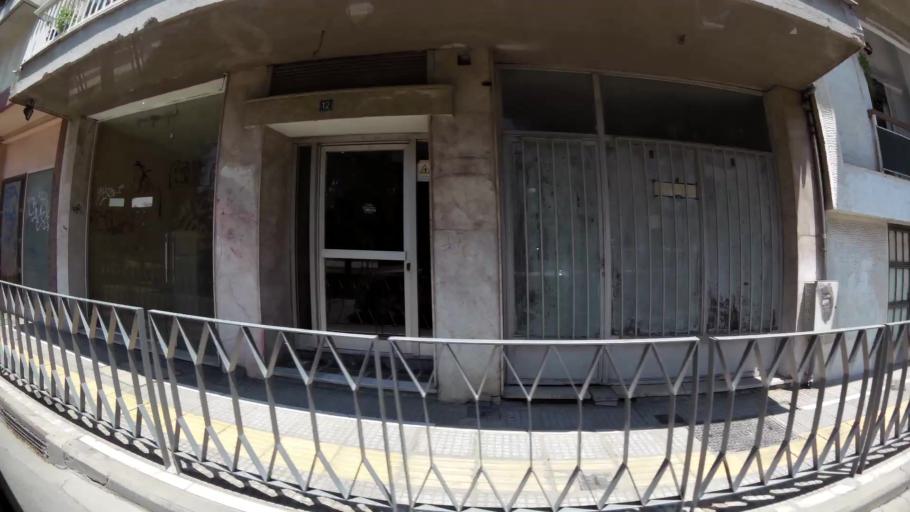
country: GR
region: Central Macedonia
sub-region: Nomos Thessalonikis
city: Ampelokipoi
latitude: 40.6498
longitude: 22.9218
